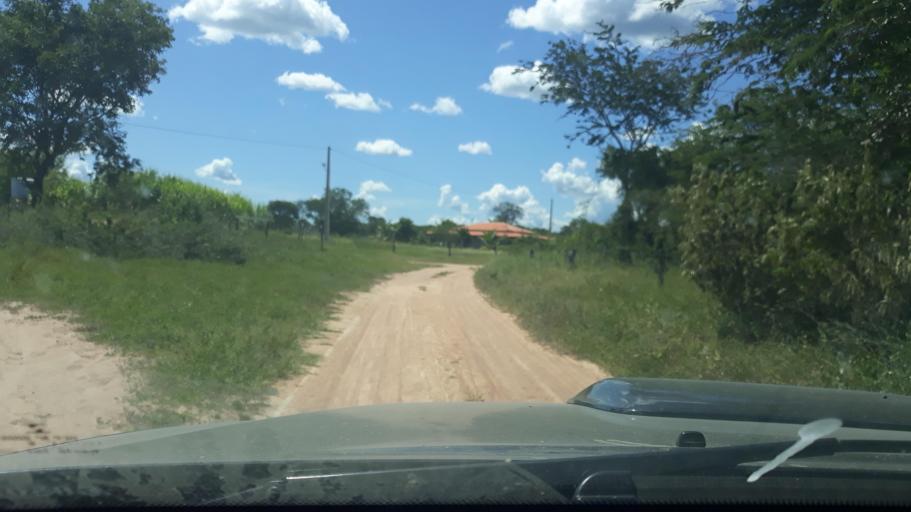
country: BR
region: Bahia
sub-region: Riacho De Santana
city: Riacho de Santana
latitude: -13.8691
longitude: -43.0185
